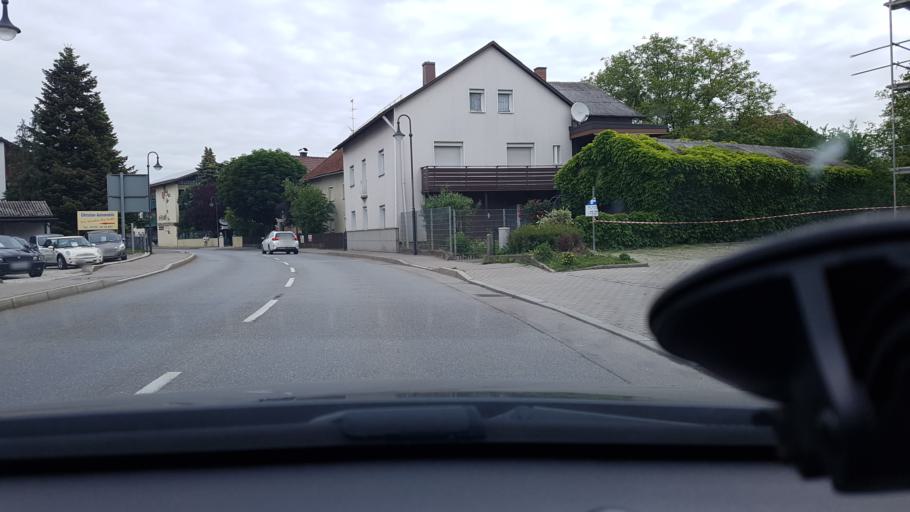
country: DE
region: Bavaria
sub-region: Lower Bavaria
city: Pocking
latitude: 48.3981
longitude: 13.3113
